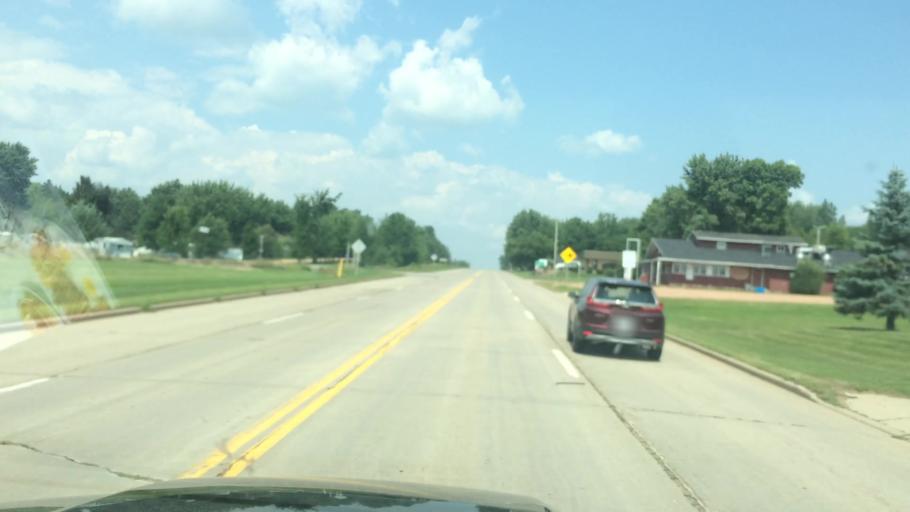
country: US
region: Wisconsin
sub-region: Clark County
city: Colby
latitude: 44.8454
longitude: -90.3160
